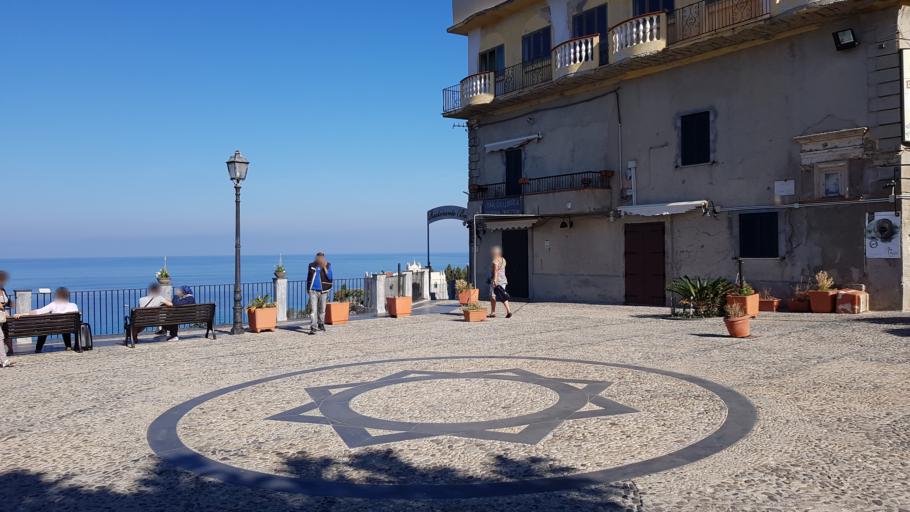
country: IT
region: Calabria
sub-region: Provincia di Vibo-Valentia
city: Tropea
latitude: 38.6783
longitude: 15.8958
